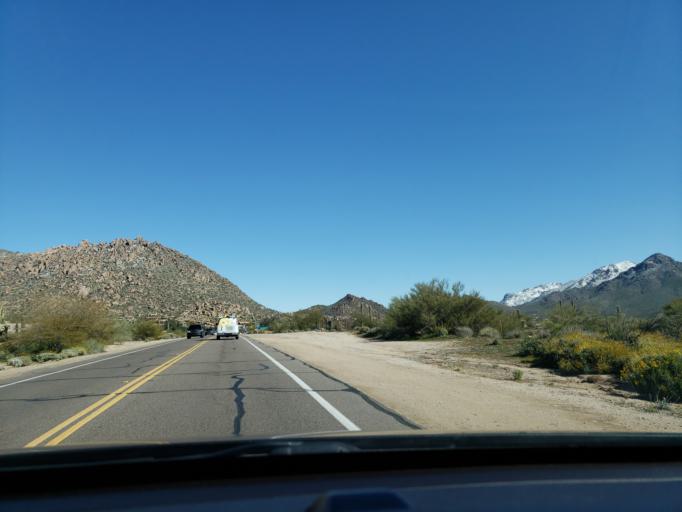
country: US
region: Arizona
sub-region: Maricopa County
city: Carefree
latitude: 33.7126
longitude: -111.8602
